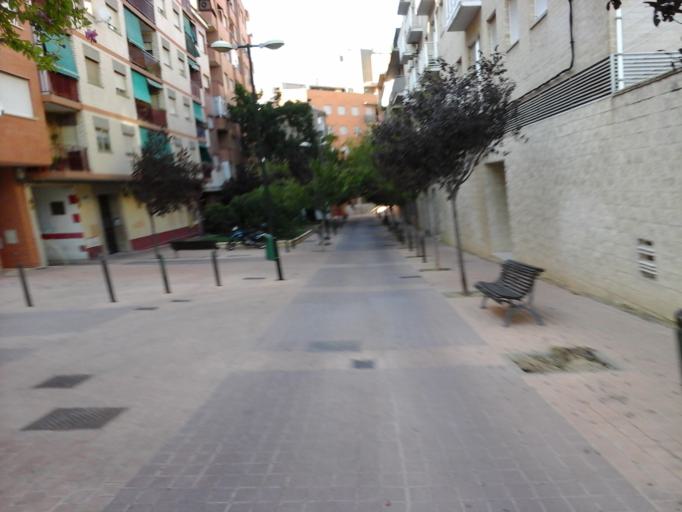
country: ES
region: Aragon
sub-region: Provincia de Zaragoza
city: Zaragoza
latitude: 41.6309
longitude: -0.8769
